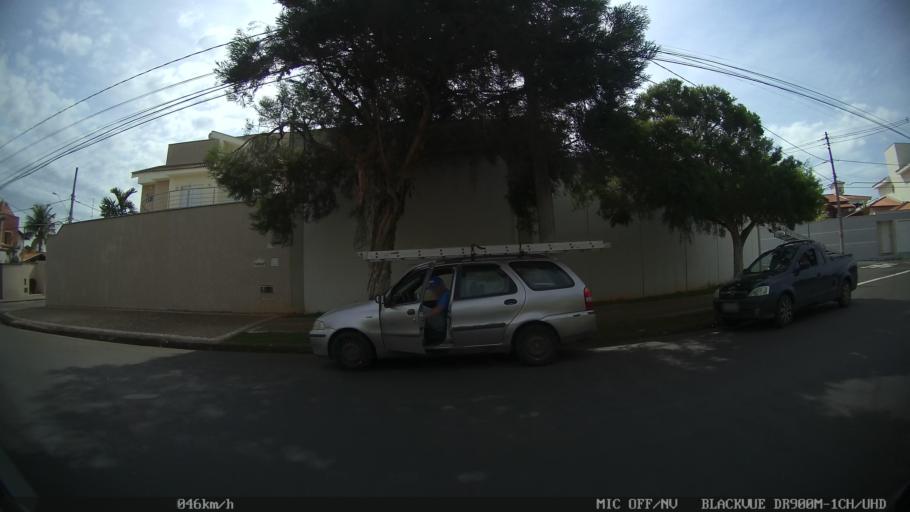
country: BR
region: Sao Paulo
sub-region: Piracicaba
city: Piracicaba
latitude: -22.7156
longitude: -47.6687
